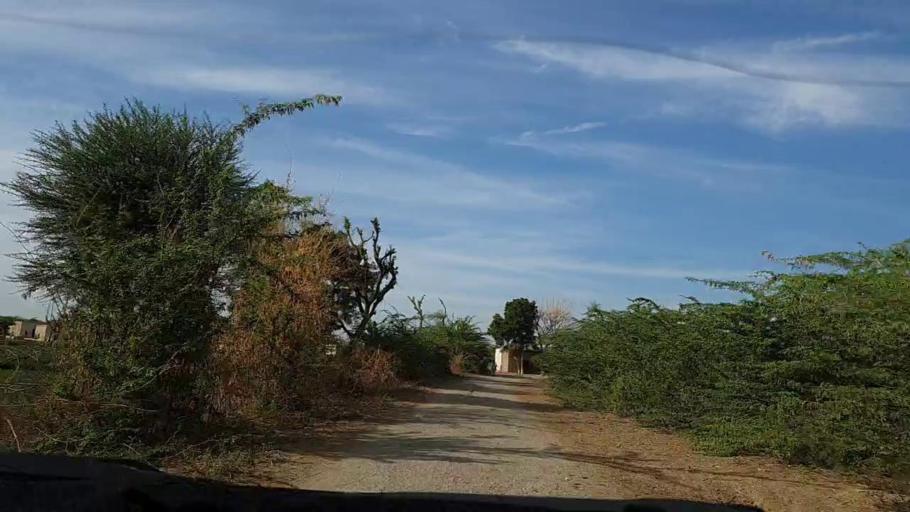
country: PK
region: Sindh
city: Dhoro Naro
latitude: 25.4986
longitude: 69.5427
